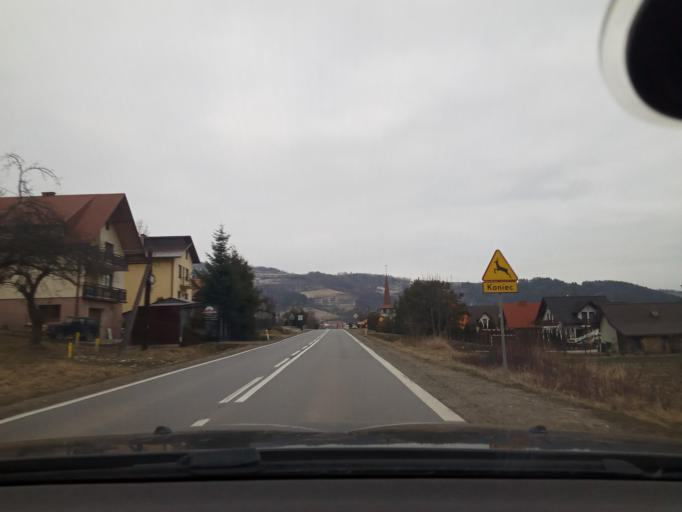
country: PL
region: Lesser Poland Voivodeship
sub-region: Powiat nowosadecki
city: Lacko
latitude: 49.5373
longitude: 20.4054
